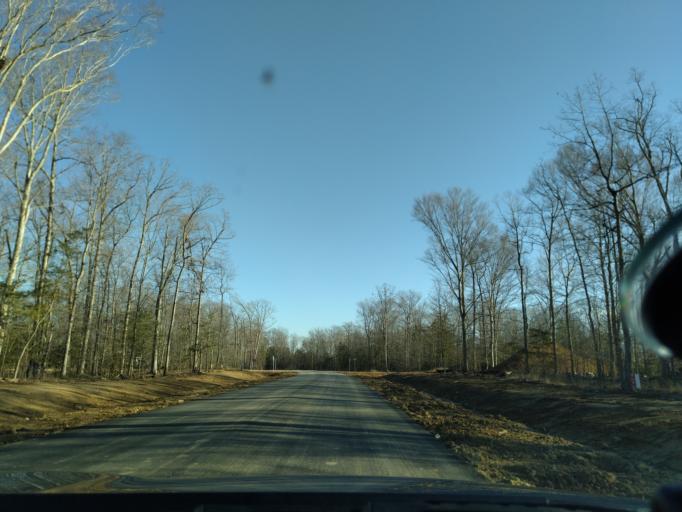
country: US
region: Maryland
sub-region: Charles County
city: La Plata
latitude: 38.4919
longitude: -76.8911
